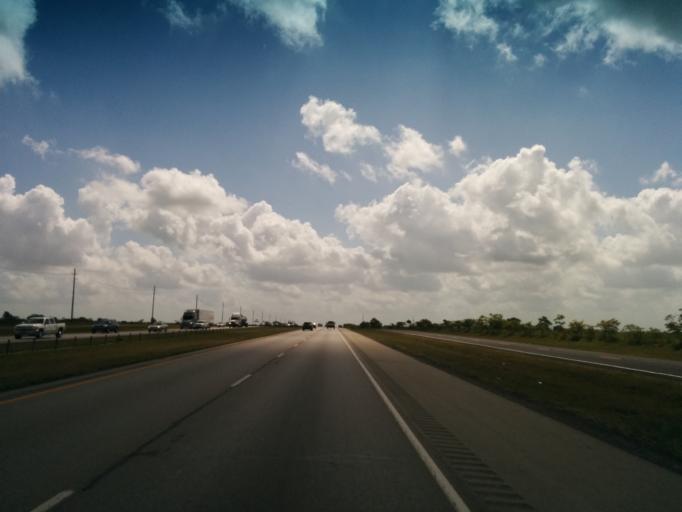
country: US
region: Texas
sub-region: Austin County
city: Sealy
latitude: 29.7561
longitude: -96.2381
